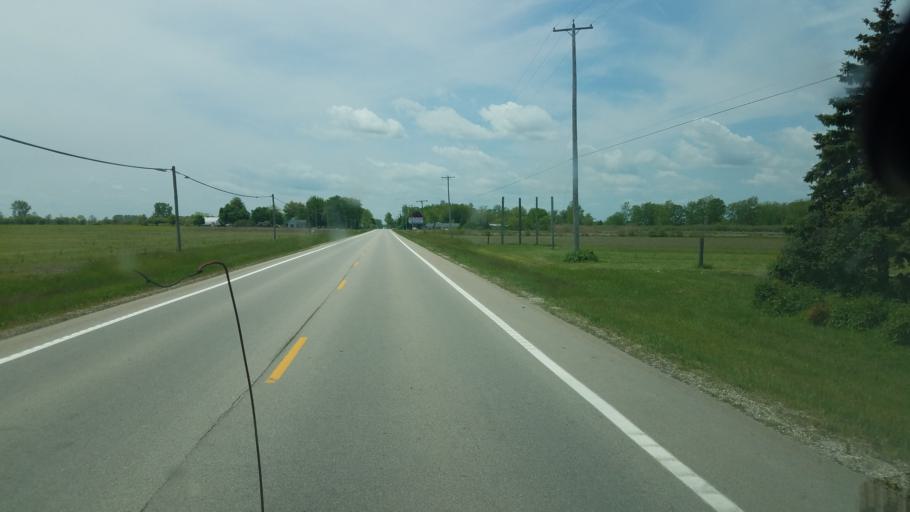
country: US
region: Ohio
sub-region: Ottawa County
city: Port Clinton
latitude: 41.4845
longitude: -83.0060
